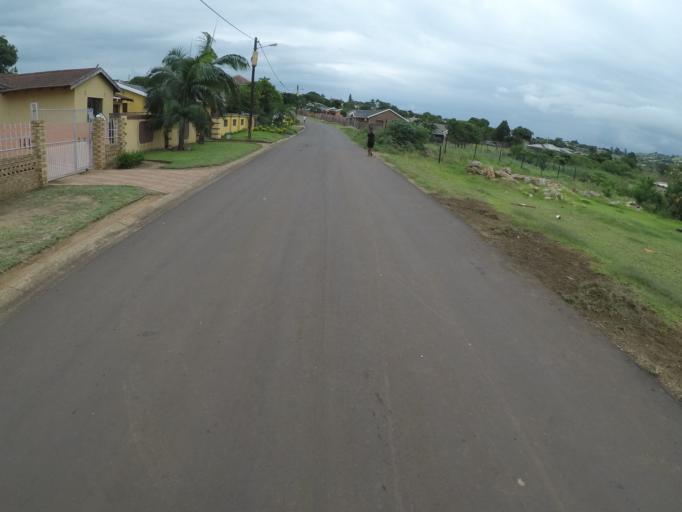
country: ZA
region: KwaZulu-Natal
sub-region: uThungulu District Municipality
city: Empangeni
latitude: -28.7768
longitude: 31.8560
